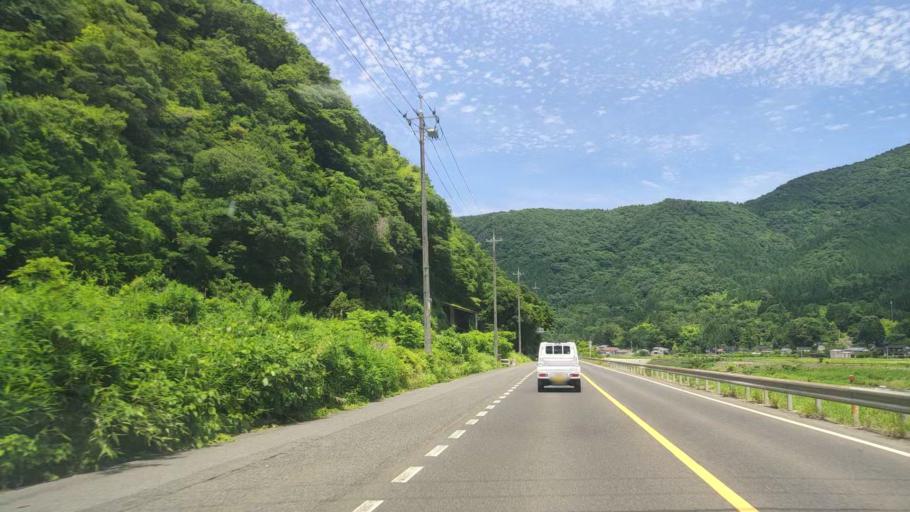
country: JP
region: Tottori
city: Tottori
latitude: 35.3625
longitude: 134.3782
